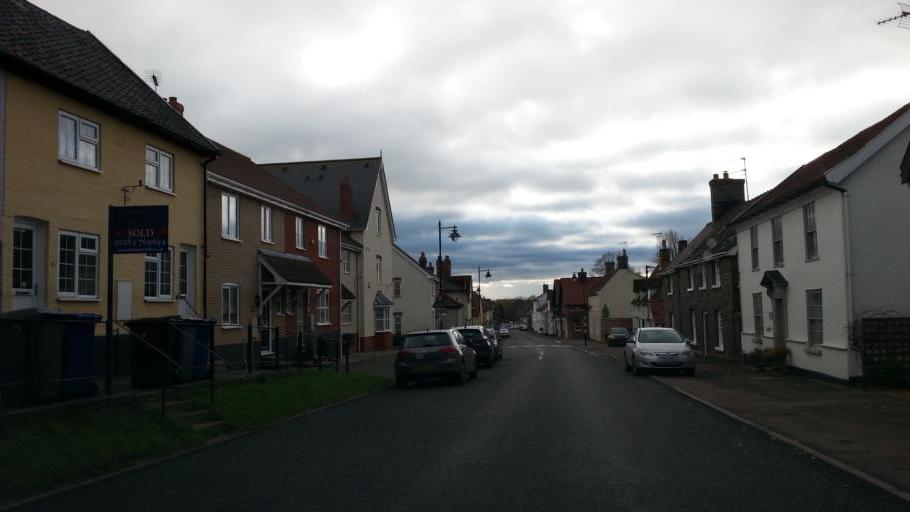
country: GB
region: England
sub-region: Suffolk
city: Ixworth
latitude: 52.3005
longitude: 0.8347
